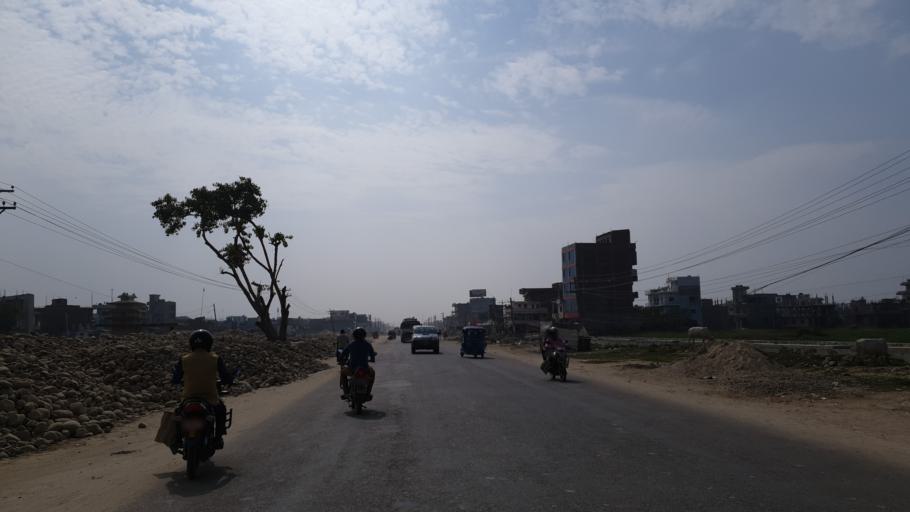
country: NP
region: Central Region
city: Janakpur
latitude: 26.7481
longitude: 85.9237
